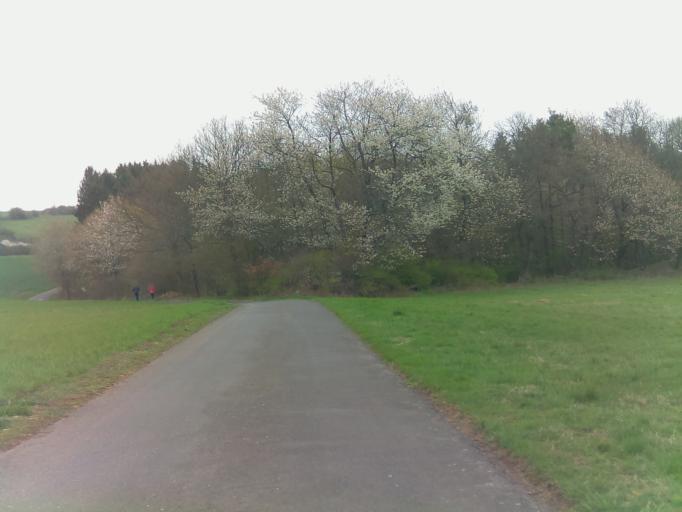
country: DE
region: Rheinland-Pfalz
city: Gerach
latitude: 49.7483
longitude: 7.3196
